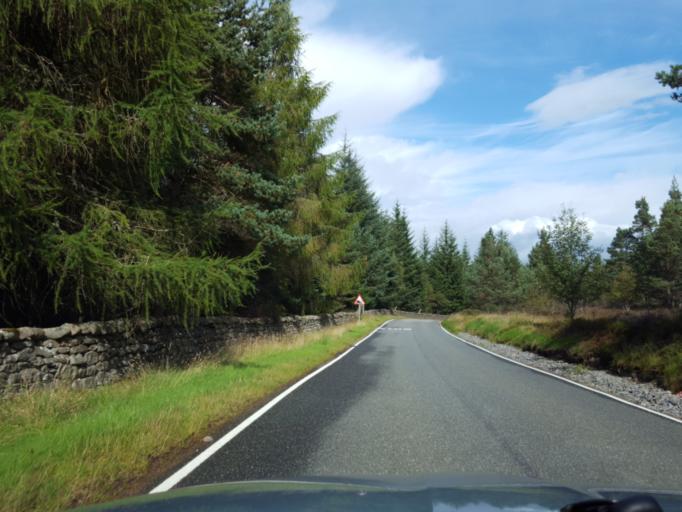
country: GB
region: Scotland
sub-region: Aberdeenshire
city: Banchory
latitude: 56.9576
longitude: -2.5809
